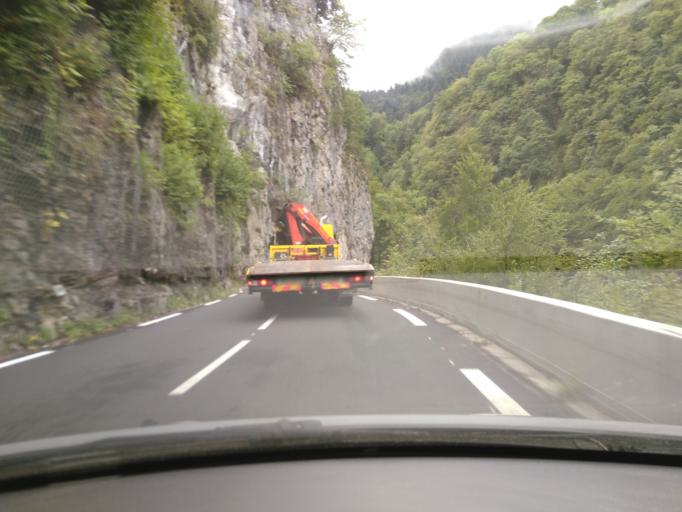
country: FR
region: Rhone-Alpes
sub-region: Departement de la Haute-Savoie
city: Bonneville
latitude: 46.0362
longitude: 6.3837
